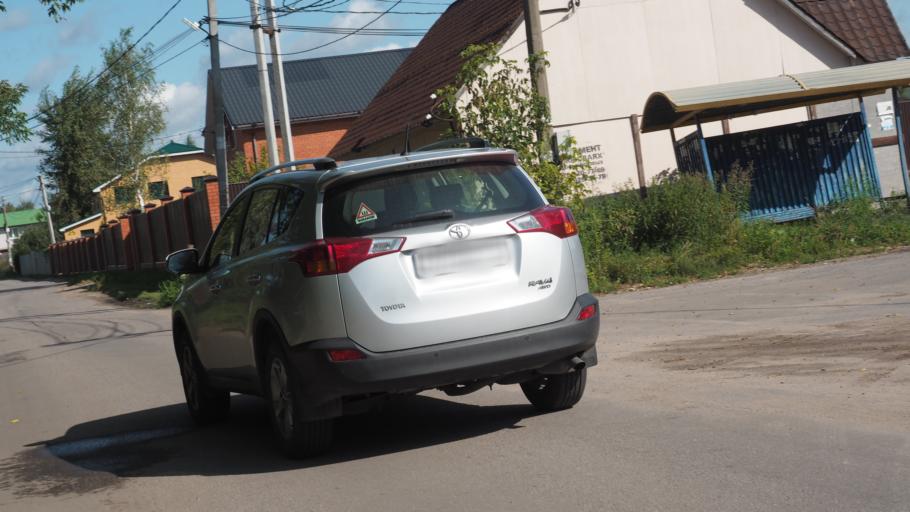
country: RU
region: Moskovskaya
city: Ramenskoye
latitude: 55.5769
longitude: 38.3020
